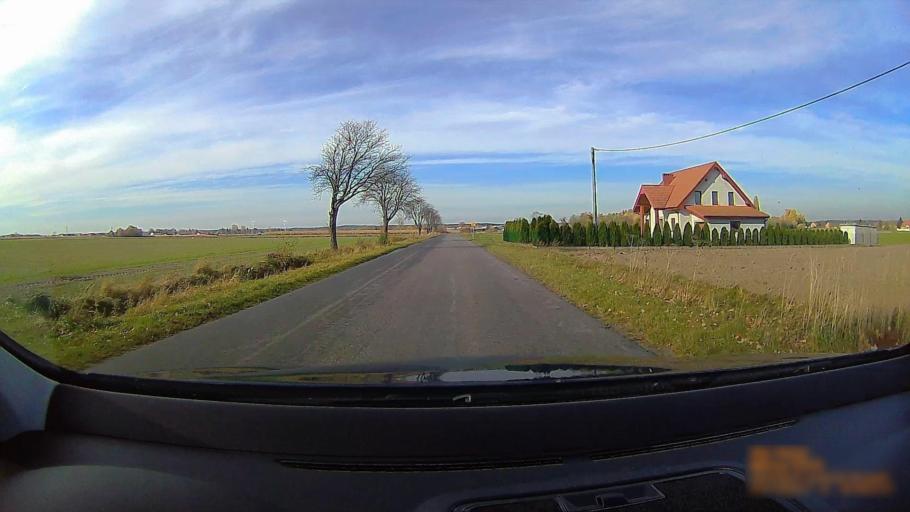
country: PL
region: Greater Poland Voivodeship
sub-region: Powiat ostrzeszowski
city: Doruchow
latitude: 51.4237
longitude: 18.0576
